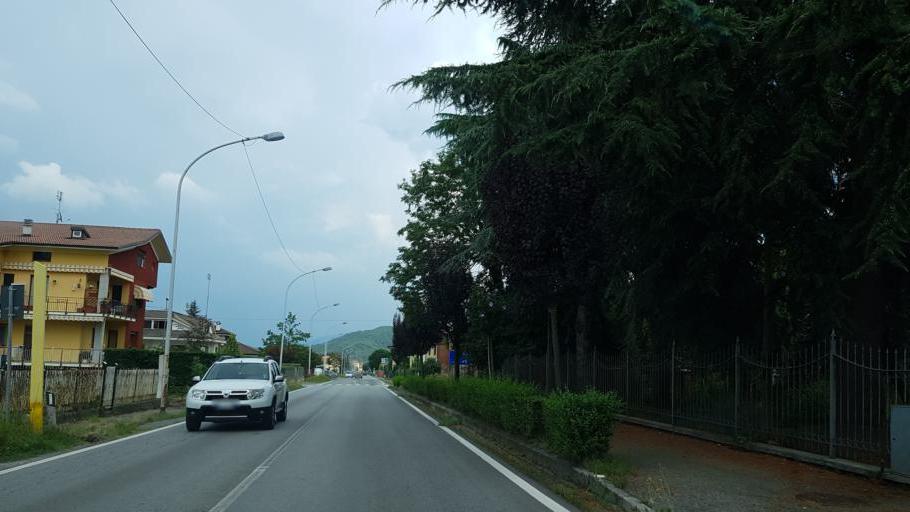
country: IT
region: Piedmont
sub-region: Provincia di Cuneo
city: Roccavione
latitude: 44.3329
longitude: 7.4724
